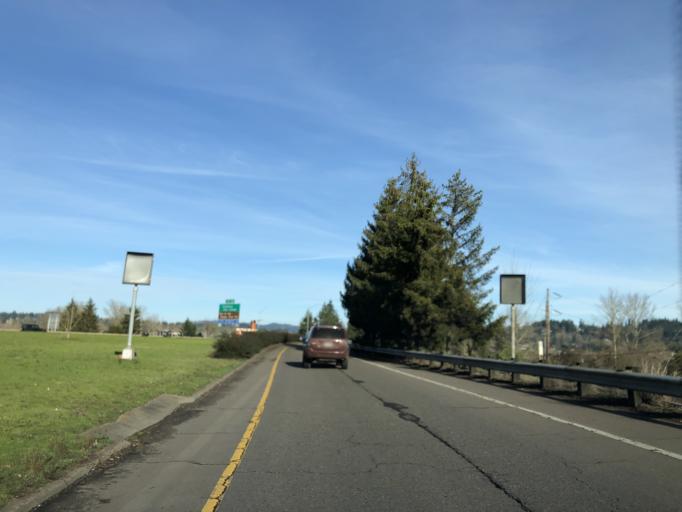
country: US
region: Oregon
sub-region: Clackamas County
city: Oregon City
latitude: 45.3647
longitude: -122.5993
